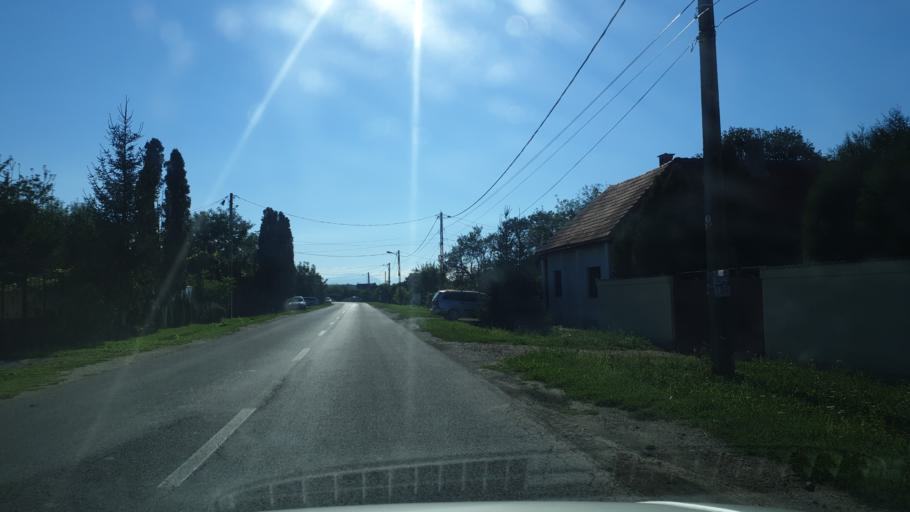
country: RO
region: Covasna
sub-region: Comuna Ilieni
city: Ilieni
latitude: 45.7637
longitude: 25.7255
